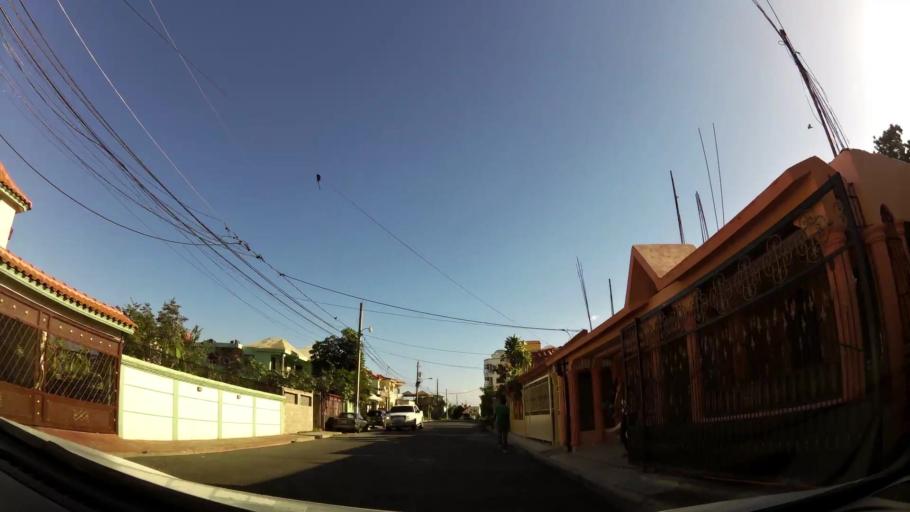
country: DO
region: Santo Domingo
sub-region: Santo Domingo
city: Santo Domingo Este
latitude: 18.4882
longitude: -69.8056
